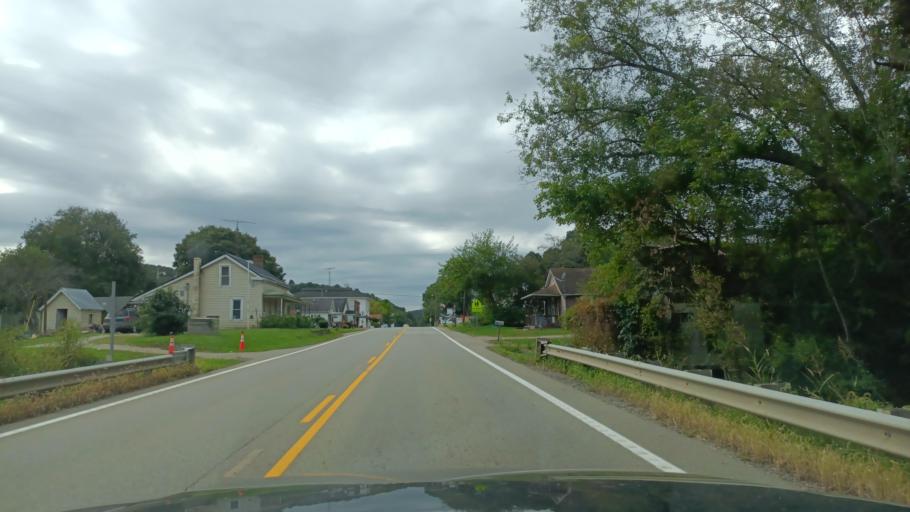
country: US
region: Ohio
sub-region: Vinton County
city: McArthur
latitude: 39.2726
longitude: -82.6049
